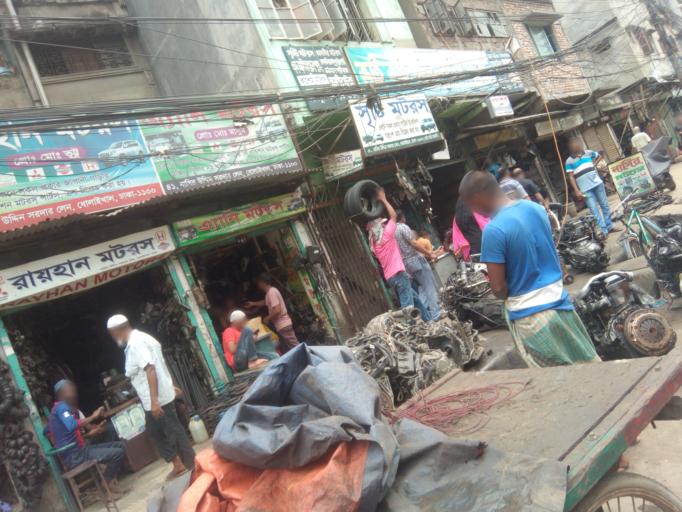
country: BD
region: Dhaka
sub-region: Dhaka
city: Dhaka
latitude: 23.7137
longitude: 90.4130
